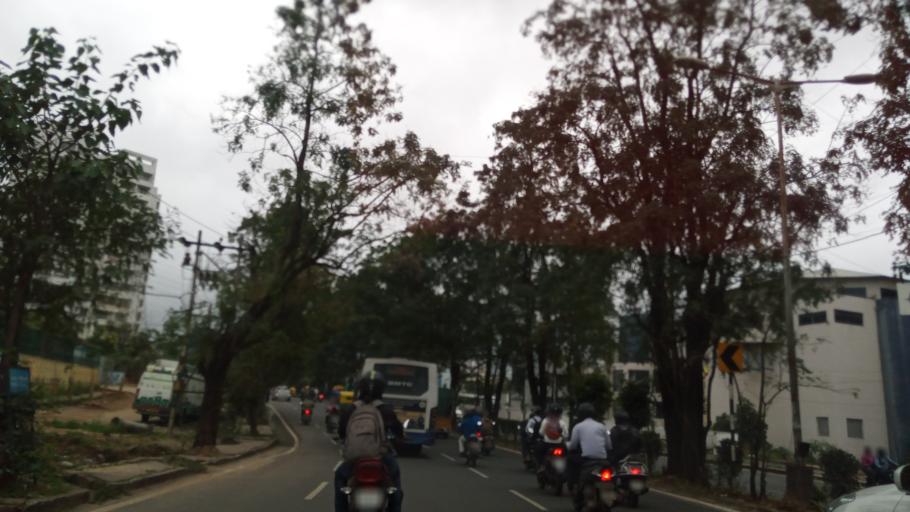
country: IN
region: Karnataka
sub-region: Bangalore Urban
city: Bangalore
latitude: 12.9365
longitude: 77.5344
